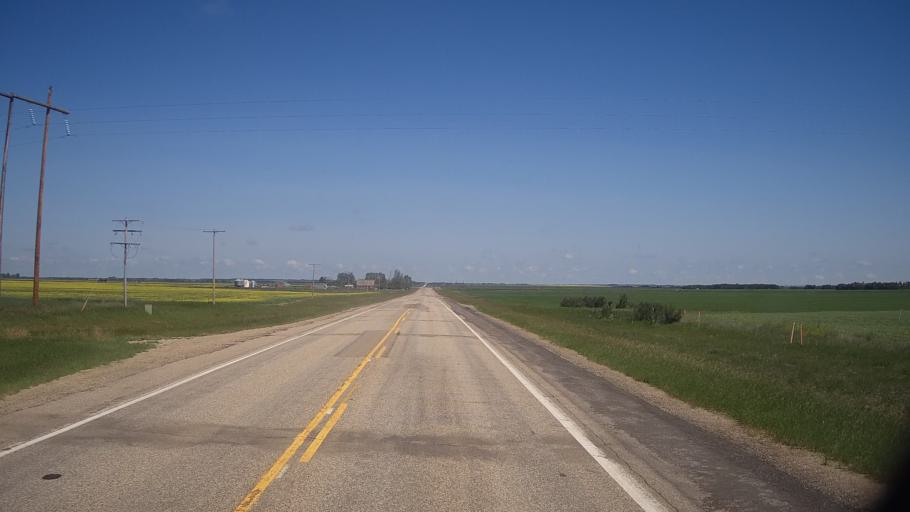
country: CA
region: Saskatchewan
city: Saskatoon
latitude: 51.9826
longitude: -106.0754
